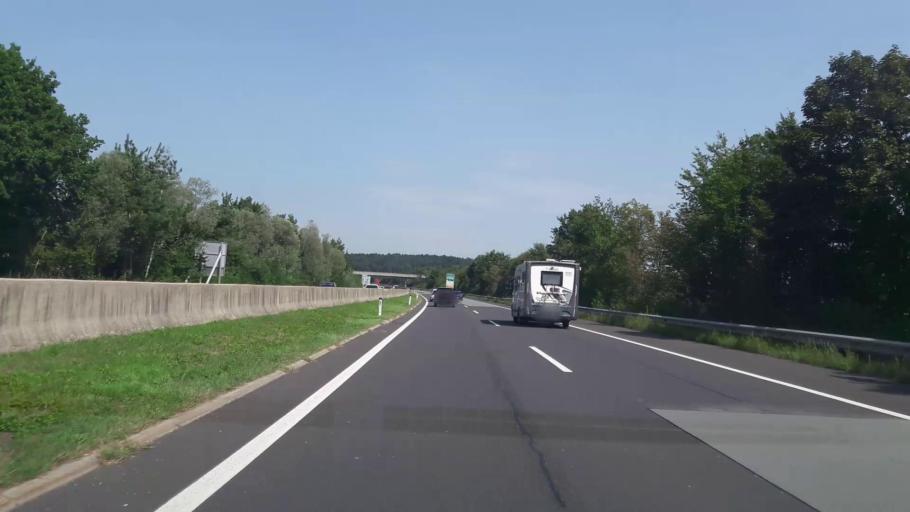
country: AT
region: Burgenland
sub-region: Politischer Bezirk Oberwart
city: Markt Allhau
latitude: 47.2869
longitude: 16.0676
